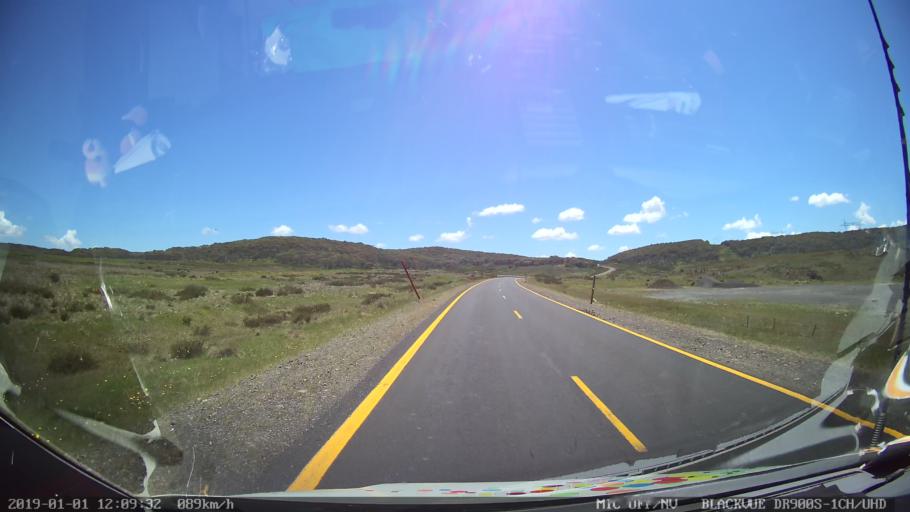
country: AU
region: New South Wales
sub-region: Tumut Shire
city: Tumut
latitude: -35.8059
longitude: 148.4960
